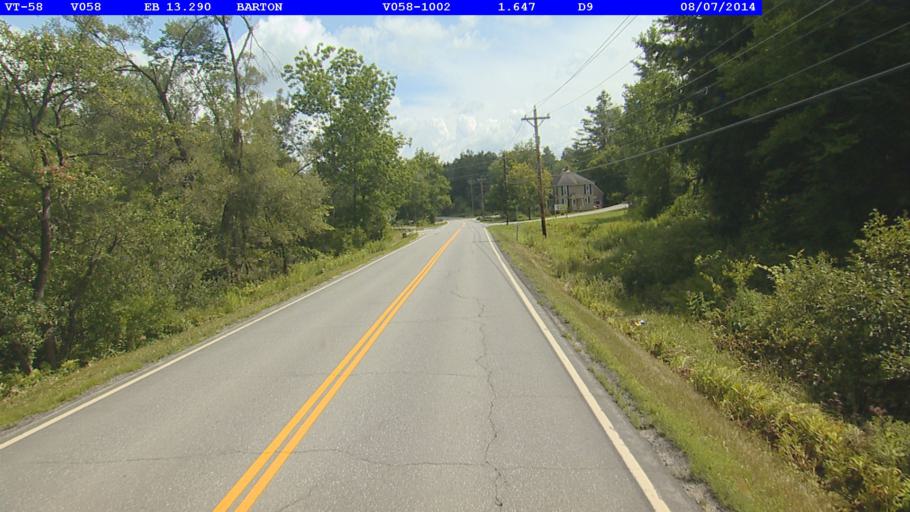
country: US
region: Vermont
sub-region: Orleans County
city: Newport
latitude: 44.8027
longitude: -72.1807
